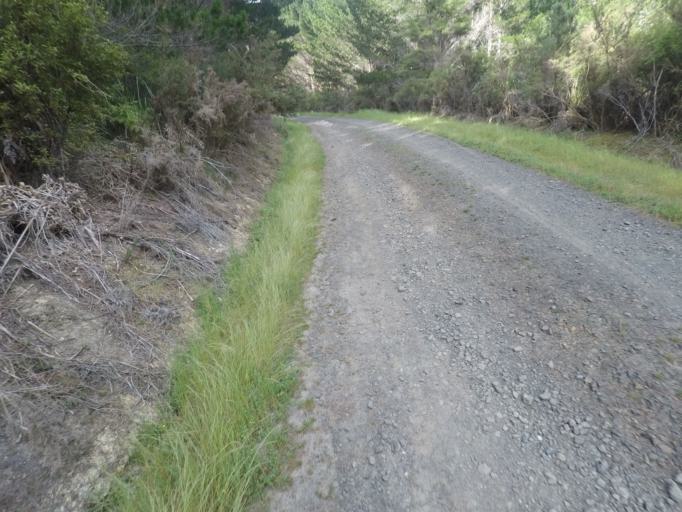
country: NZ
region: Auckland
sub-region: Auckland
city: Muriwai Beach
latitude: -36.7413
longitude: 174.5719
